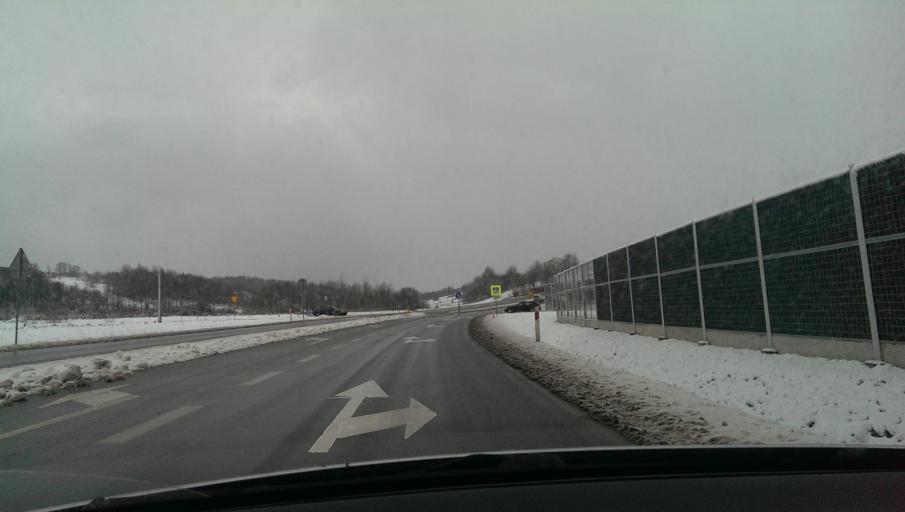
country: PL
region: Subcarpathian Voivodeship
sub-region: Powiat brzozowski
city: Brzozow
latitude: 49.7018
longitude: 22.0348
